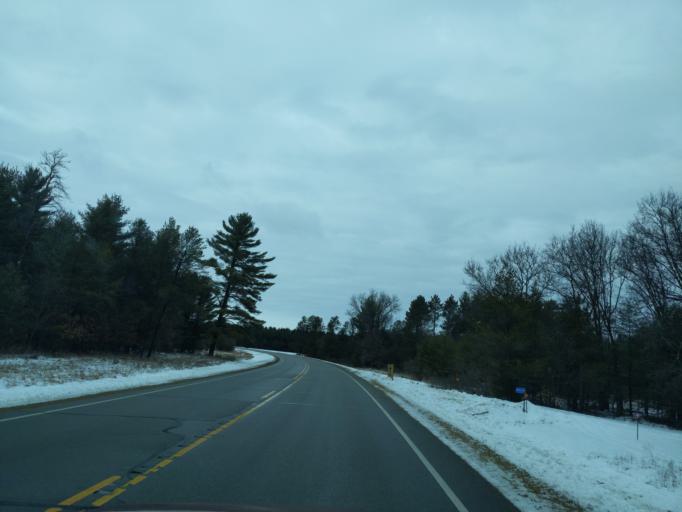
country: US
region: Wisconsin
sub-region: Waushara County
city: Wautoma
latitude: 43.9555
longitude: -89.3175
